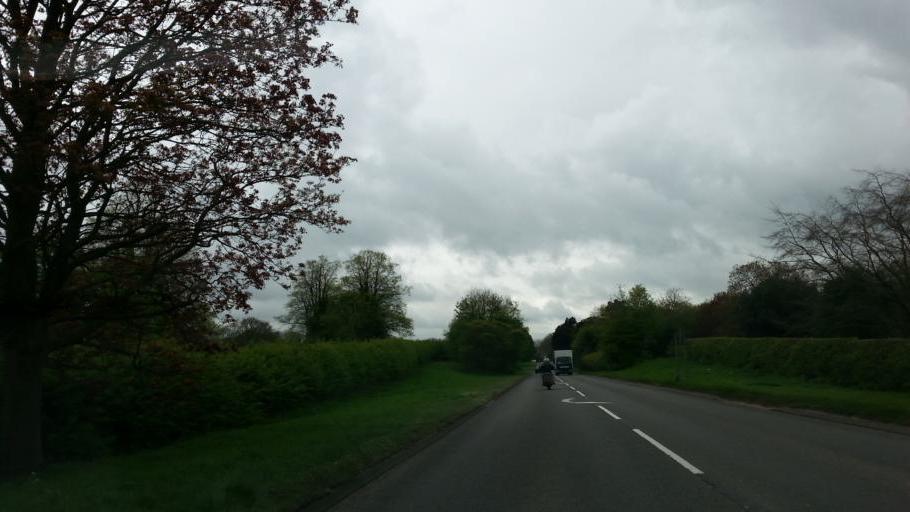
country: GB
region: England
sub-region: Leicestershire
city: Lutterworth
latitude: 52.4367
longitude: -1.2057
